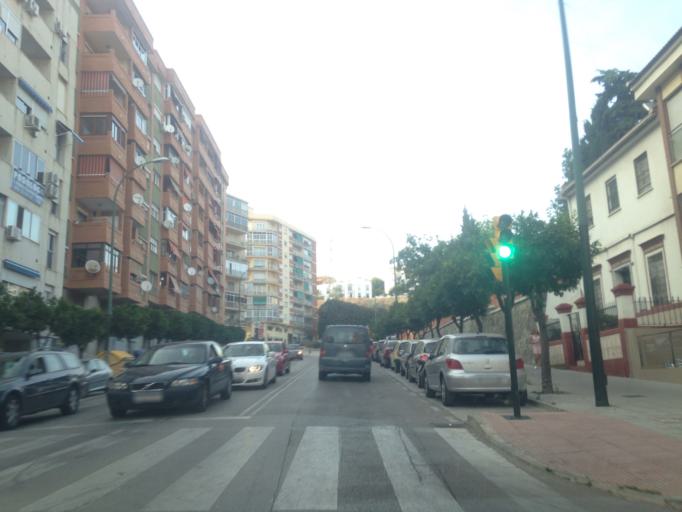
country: ES
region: Andalusia
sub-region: Provincia de Malaga
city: Malaga
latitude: 36.7351
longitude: -4.4159
